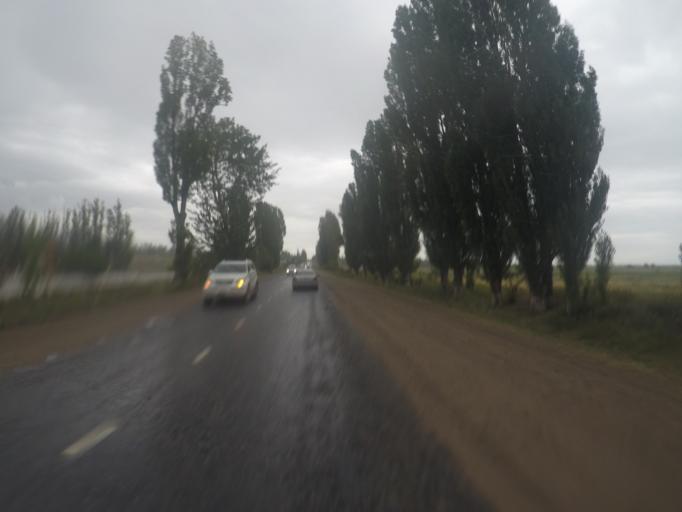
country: KG
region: Ysyk-Koel
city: Cholpon-Ata
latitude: 42.6963
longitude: 77.3984
